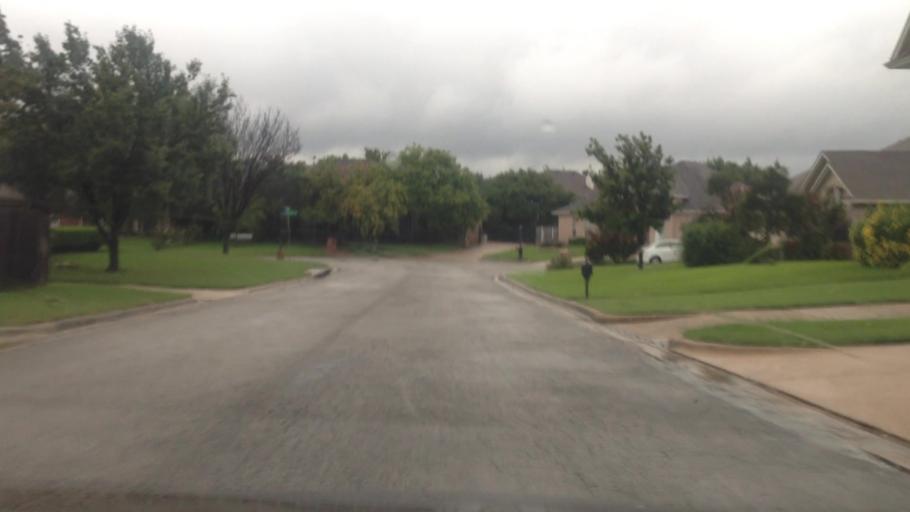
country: US
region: Texas
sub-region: Tarrant County
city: Colleyville
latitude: 32.8692
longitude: -97.1905
